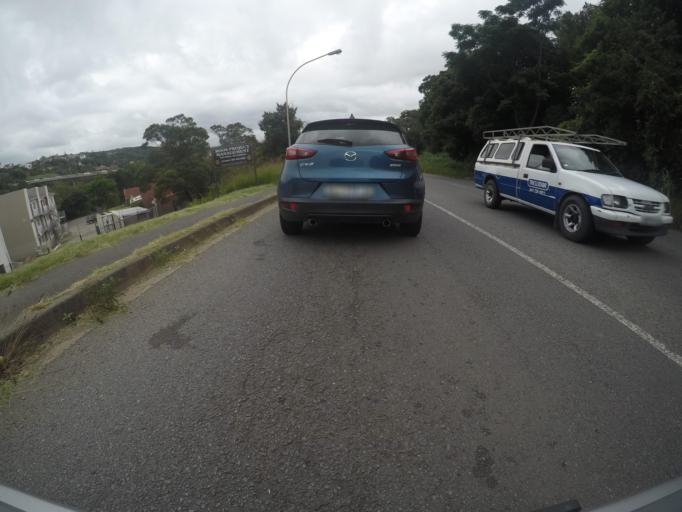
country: ZA
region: Eastern Cape
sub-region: Buffalo City Metropolitan Municipality
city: East London
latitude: -32.9779
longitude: 27.9211
